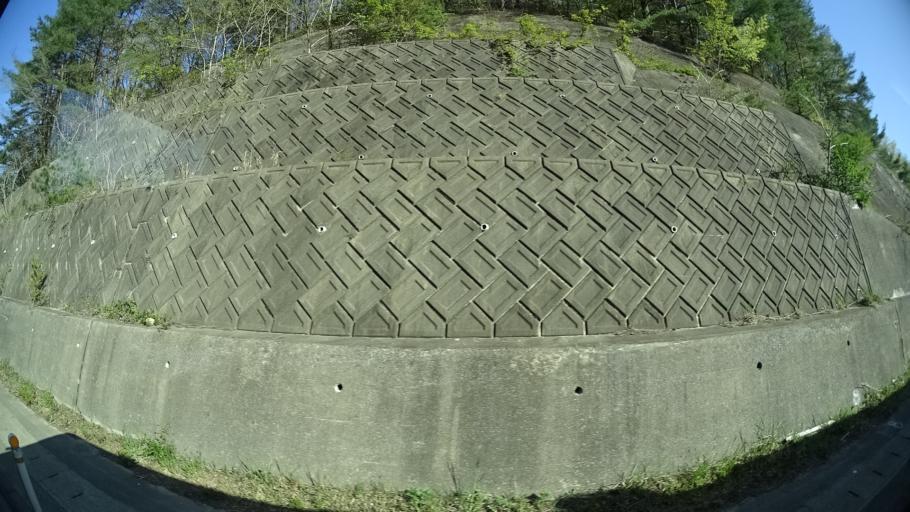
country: JP
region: Miyagi
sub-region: Oshika Gun
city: Onagawa Cho
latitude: 38.7114
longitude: 141.5104
